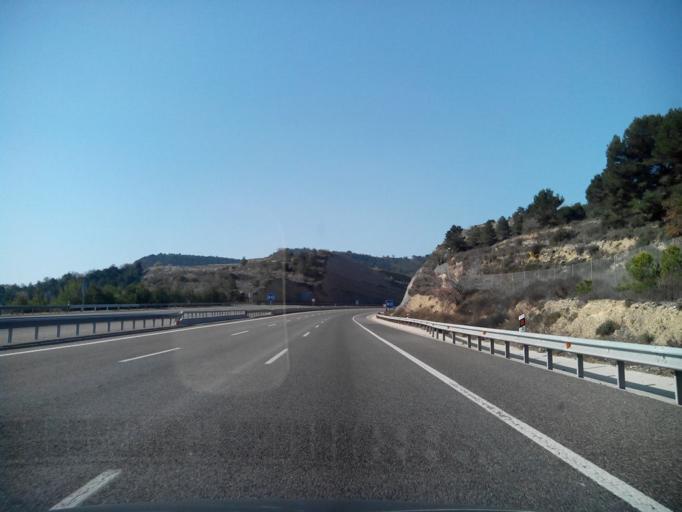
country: ES
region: Catalonia
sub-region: Provincia de Lleida
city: Sant Guim de Freixenet
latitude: 41.6241
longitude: 1.4508
